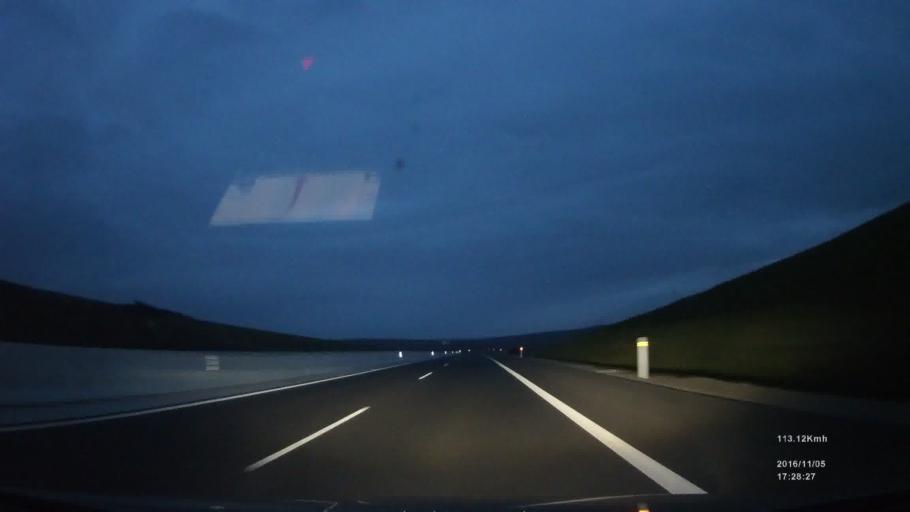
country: SK
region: Kosicky
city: Spisska Nova Ves
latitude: 49.0050
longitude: 20.4741
